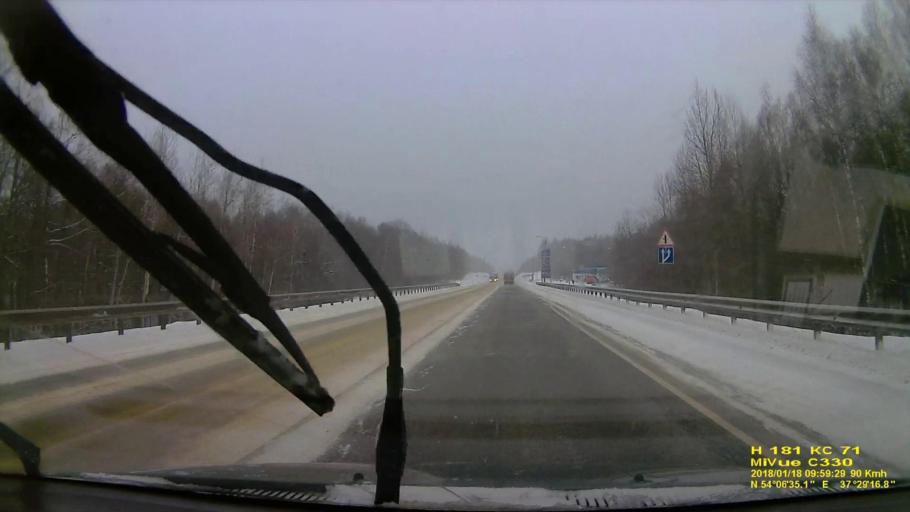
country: RU
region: Tula
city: Kosaya Gora
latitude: 54.1097
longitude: 37.4880
